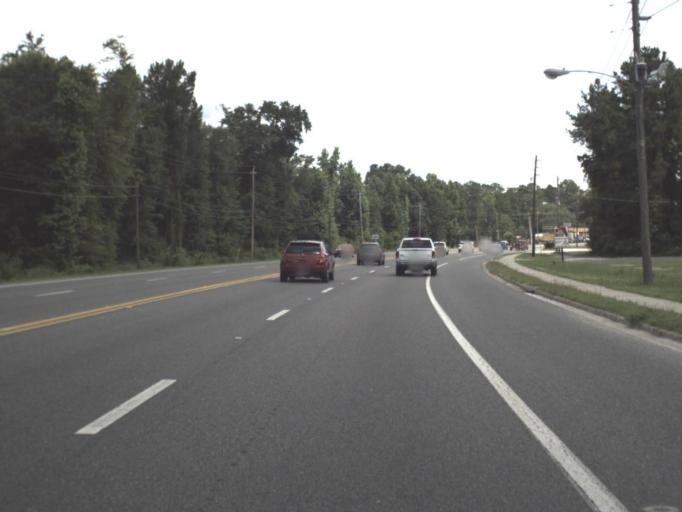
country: US
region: Florida
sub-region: Nassau County
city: Callahan
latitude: 30.5676
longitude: -81.8344
